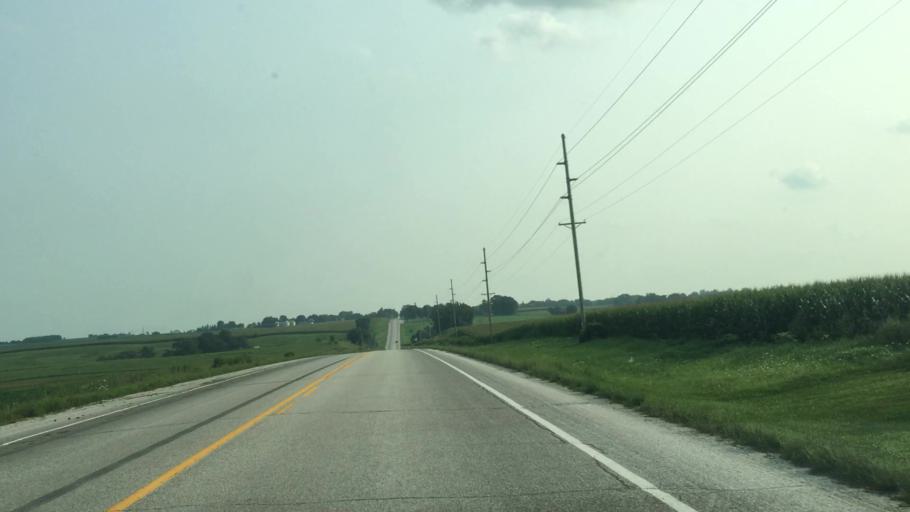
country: US
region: Minnesota
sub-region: Fillmore County
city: Harmony
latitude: 43.5493
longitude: -91.9297
